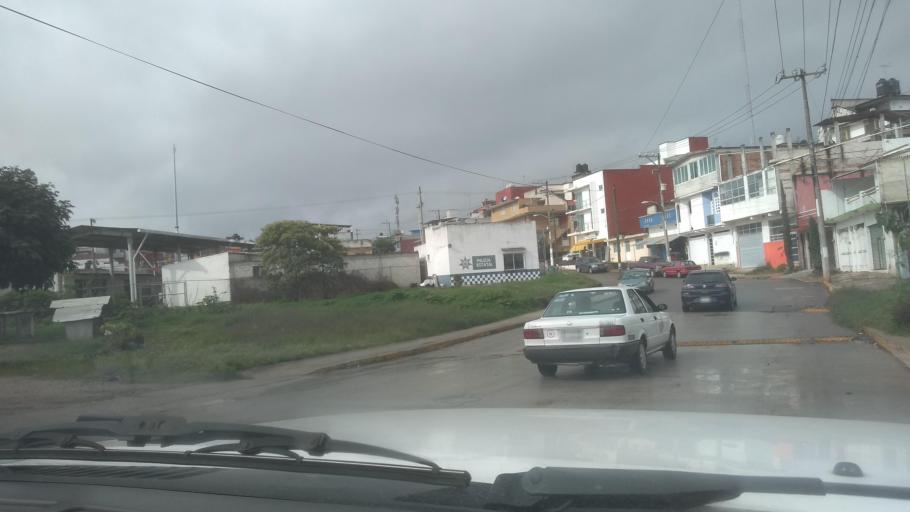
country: MX
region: Veracruz
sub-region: Xalapa
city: Colonia Santa Barbara
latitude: 19.5065
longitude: -96.8742
